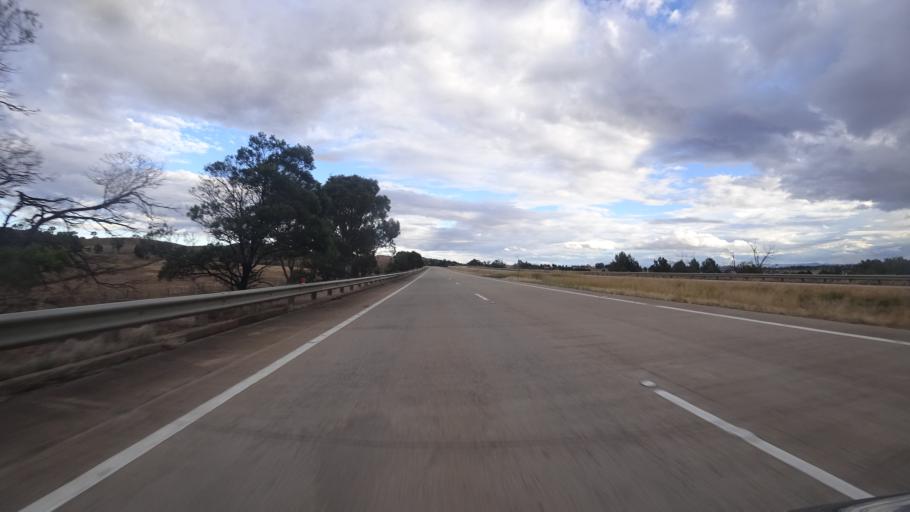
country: AU
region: New South Wales
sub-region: Yass Valley
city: Yass
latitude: -34.8211
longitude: 148.9516
